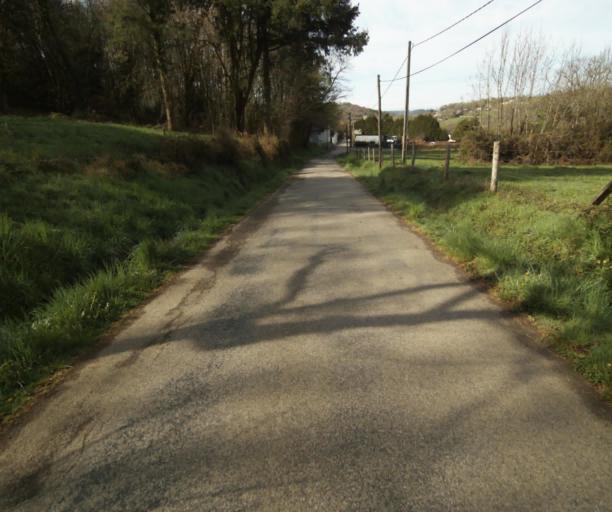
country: FR
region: Limousin
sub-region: Departement de la Correze
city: Laguenne
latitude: 45.2670
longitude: 1.8242
